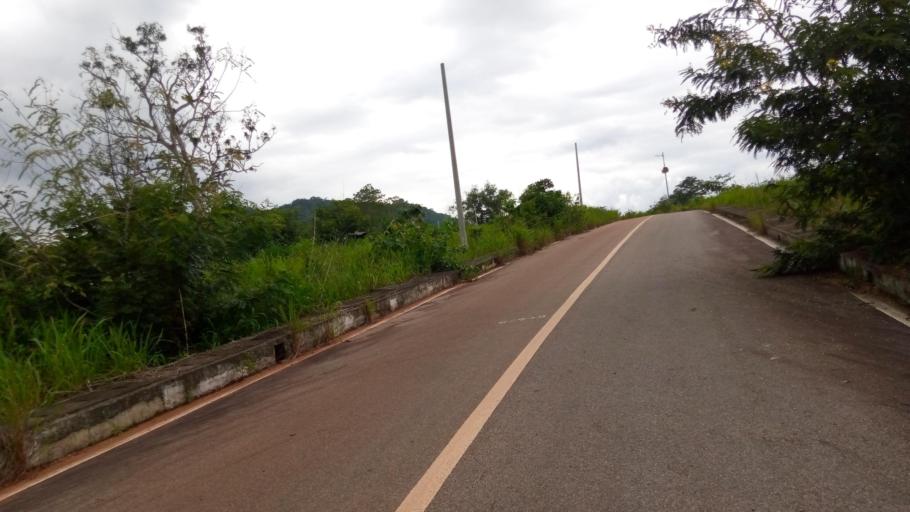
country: SL
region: Southern Province
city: Moyamba
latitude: 8.1602
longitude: -12.4429
